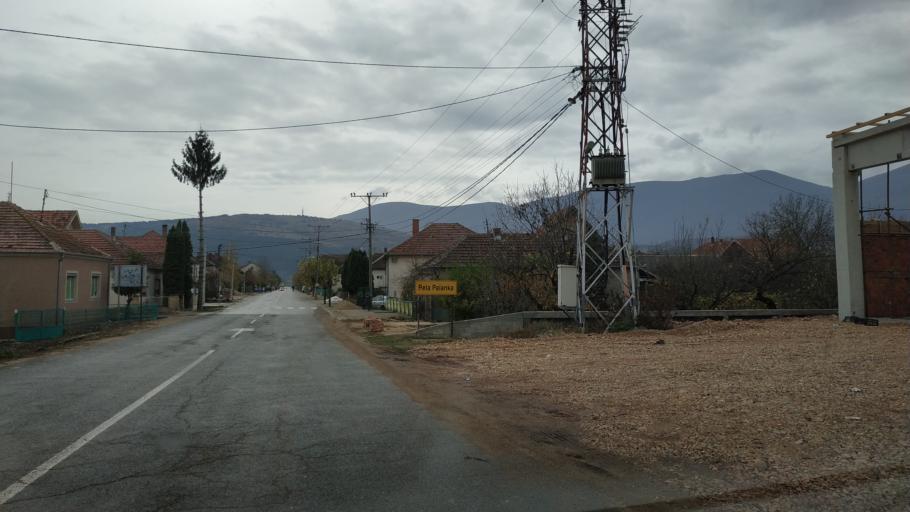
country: RS
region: Central Serbia
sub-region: Pirotski Okrug
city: Bela Palanka
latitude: 43.2296
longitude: 22.3173
